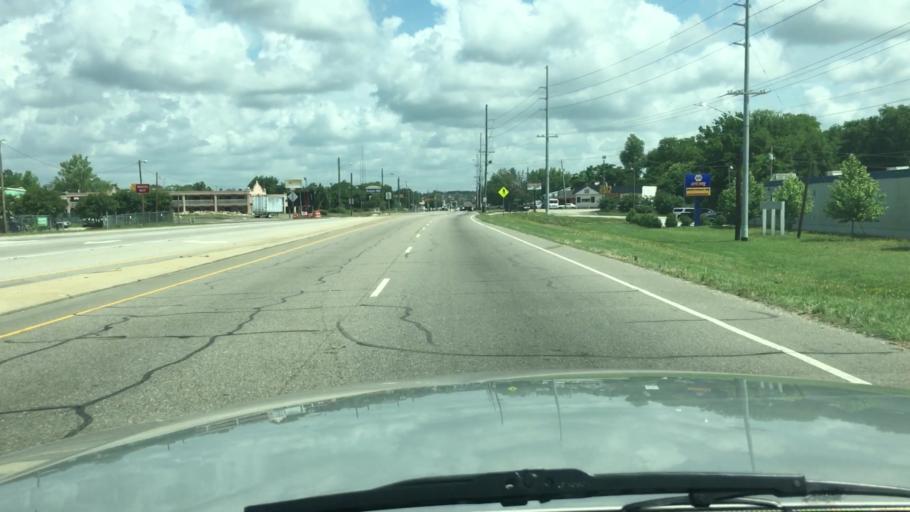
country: US
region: North Carolina
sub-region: Cumberland County
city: Fayetteville
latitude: 35.0424
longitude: -78.8660
